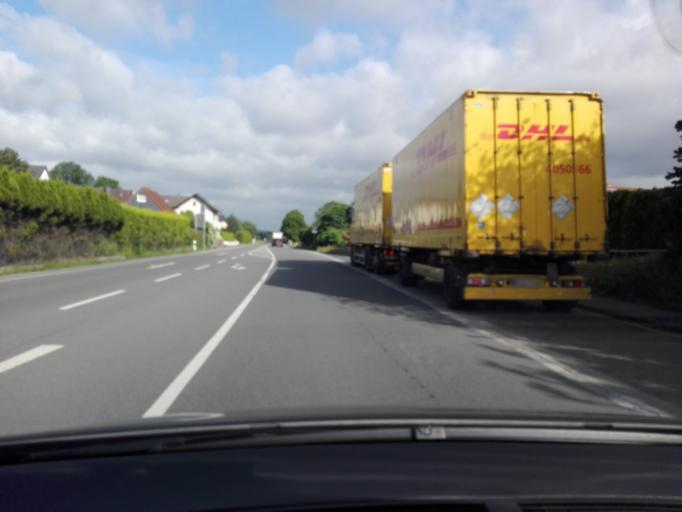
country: DE
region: North Rhine-Westphalia
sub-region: Regierungsbezirk Arnsberg
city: Menden
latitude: 51.4525
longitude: 7.7501
